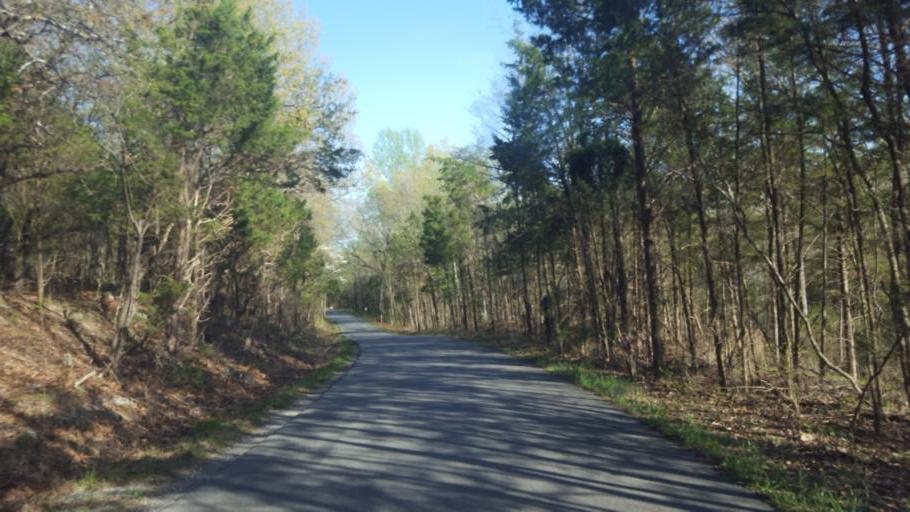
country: US
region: Kentucky
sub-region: Barren County
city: Cave City
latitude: 37.1630
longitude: -85.9792
